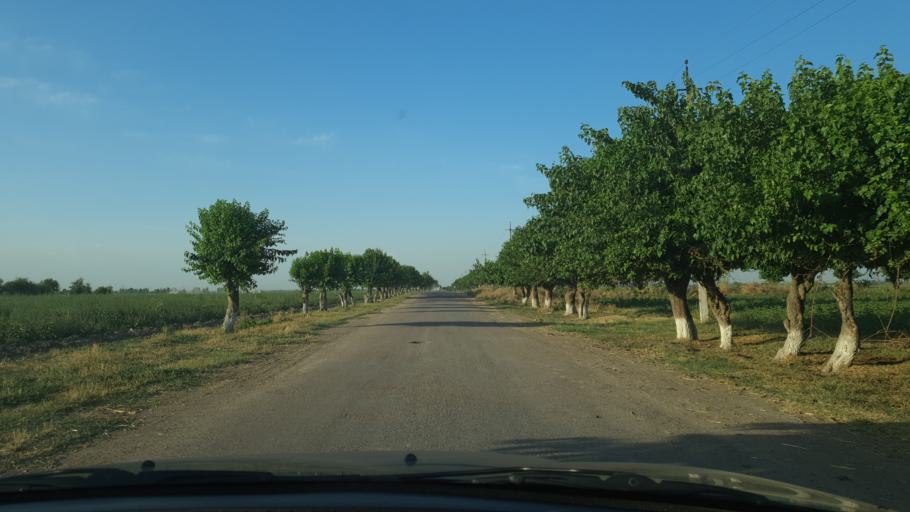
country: UZ
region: Toshkent
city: Tuytepa
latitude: 41.0908
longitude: 69.3680
